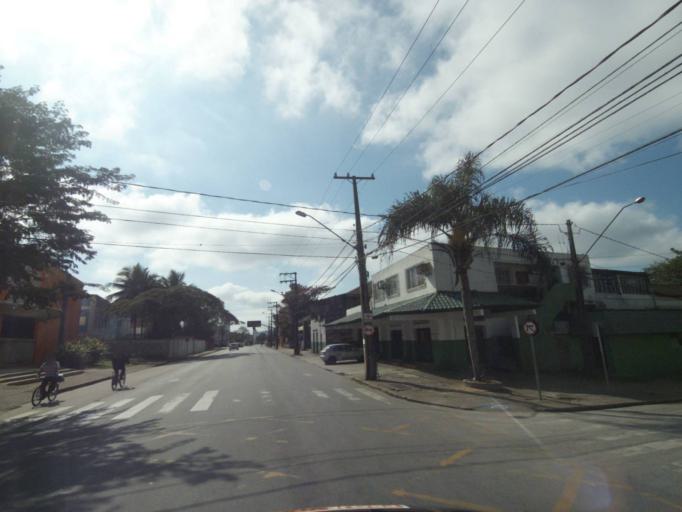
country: BR
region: Parana
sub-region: Paranagua
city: Paranagua
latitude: -25.5255
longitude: -48.5144
